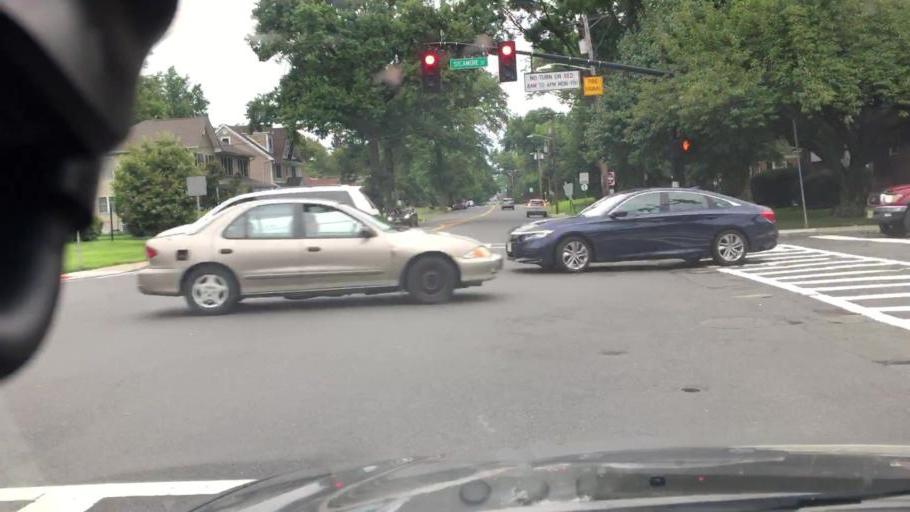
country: US
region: New Jersey
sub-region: Union County
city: Garwood
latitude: 40.6413
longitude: -74.3284
